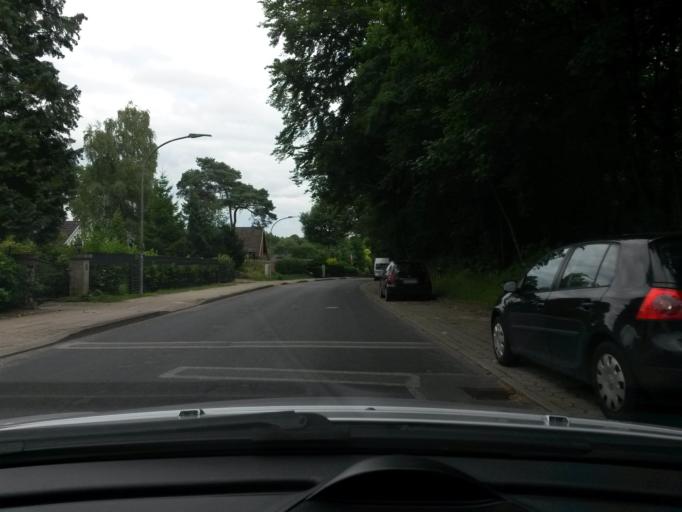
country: DE
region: Schleswig-Holstein
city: Glinde
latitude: 53.5512
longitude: 10.2063
